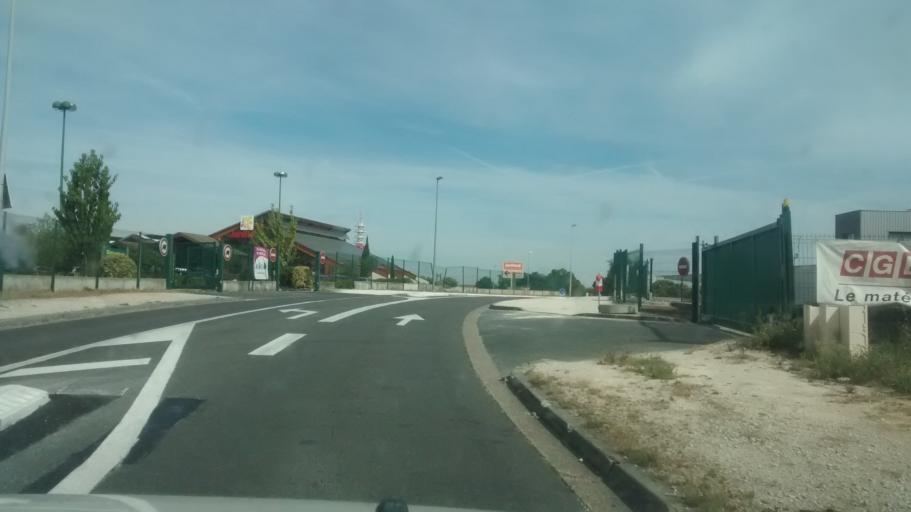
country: FR
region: Aquitaine
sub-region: Departement de la Gironde
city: Floirac
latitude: 44.8429
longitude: -0.4966
